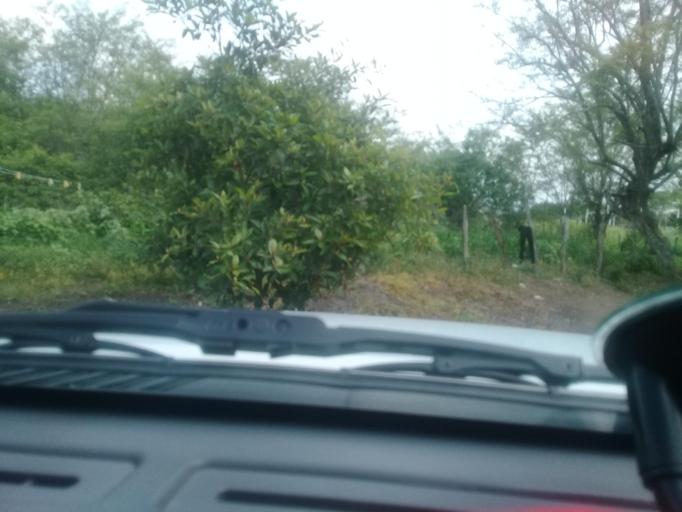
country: MX
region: Veracruz
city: Paso de Ovejas
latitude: 19.2718
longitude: -96.4195
